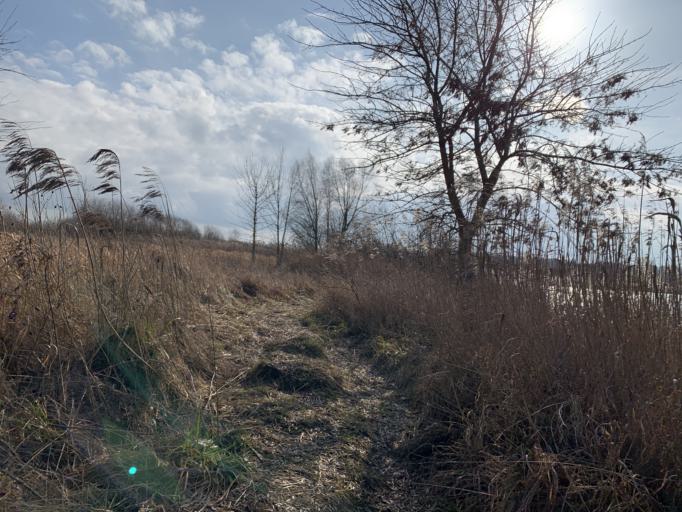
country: BY
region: Minsk
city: Nyasvizh
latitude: 53.2335
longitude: 26.7086
